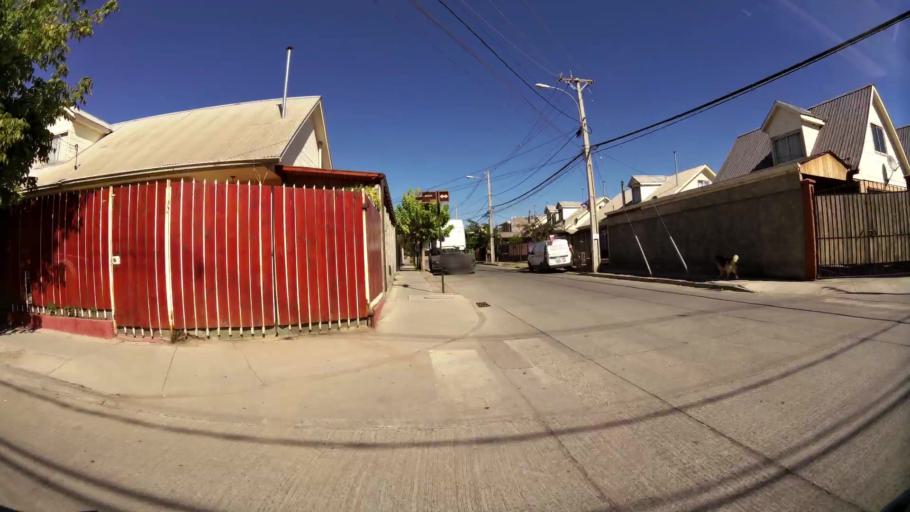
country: CL
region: O'Higgins
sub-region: Provincia de Cachapoal
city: Rancagua
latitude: -34.1823
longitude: -70.7713
